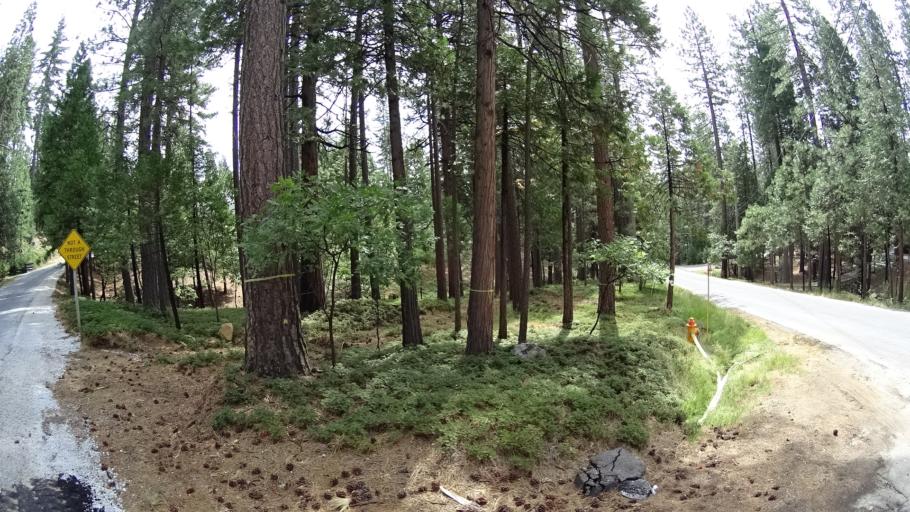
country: US
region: California
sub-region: Calaveras County
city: Arnold
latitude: 38.2490
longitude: -120.3421
